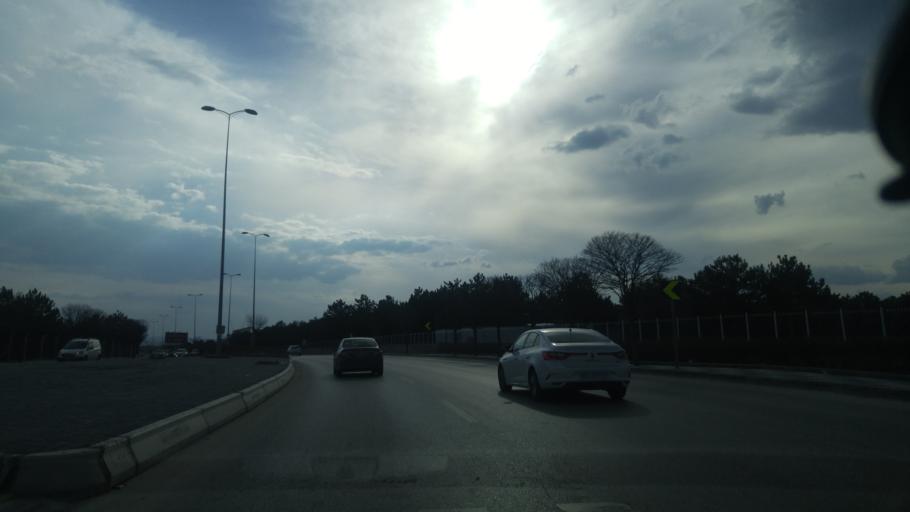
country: TR
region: Ankara
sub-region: Goelbasi
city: Golbasi
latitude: 39.8442
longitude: 32.7820
